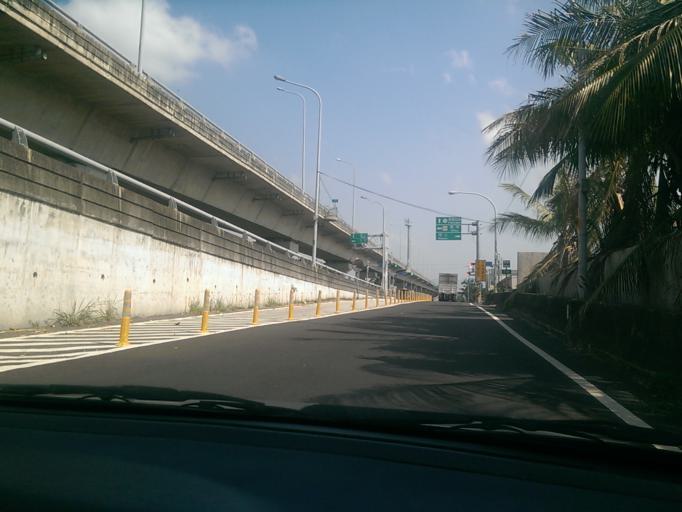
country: TW
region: Taiwan
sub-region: Changhua
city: Chang-hua
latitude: 23.9681
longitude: 120.5357
